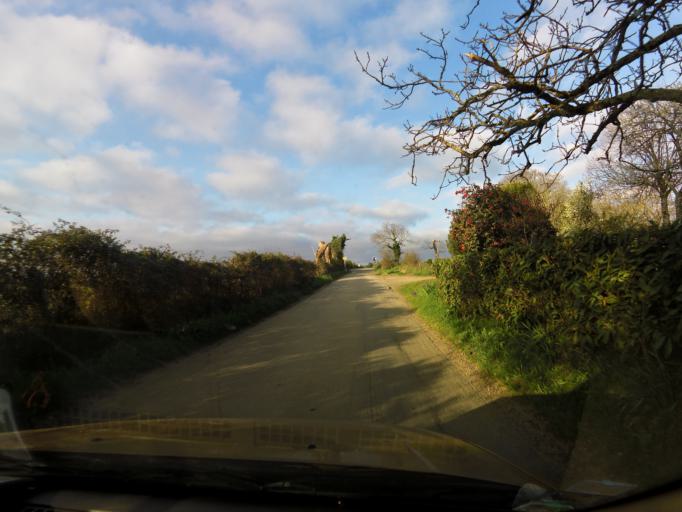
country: FR
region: Brittany
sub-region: Departement du Morbihan
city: Arradon
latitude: 47.6379
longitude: -2.8109
